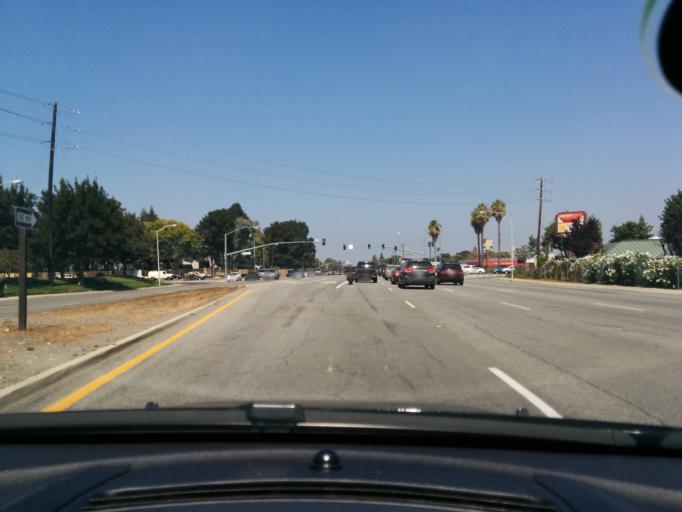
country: US
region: California
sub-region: Santa Clara County
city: Cupertino
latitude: 37.3366
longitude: -121.9956
